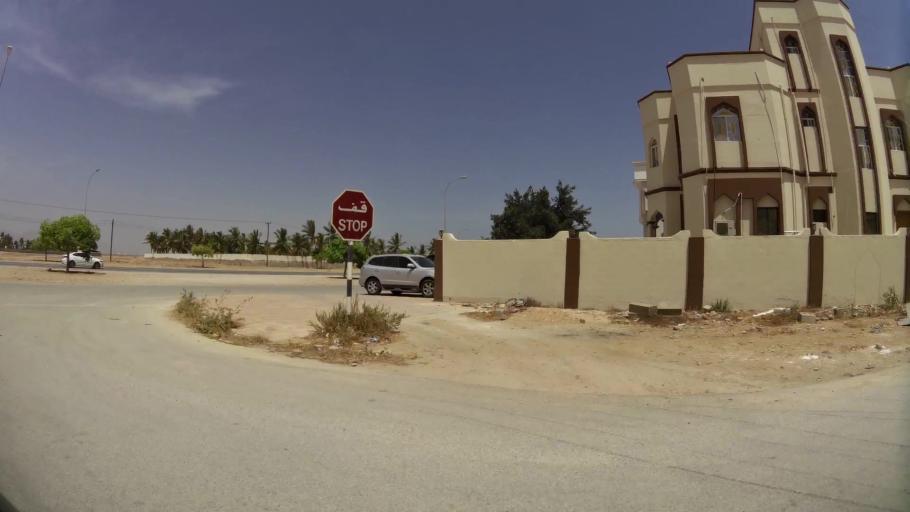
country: OM
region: Zufar
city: Salalah
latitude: 17.0627
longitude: 54.1606
